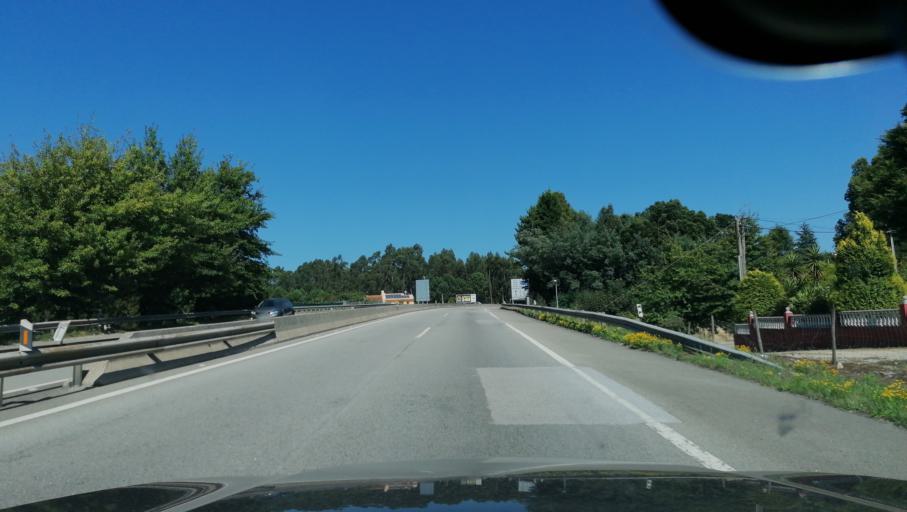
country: PT
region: Aveiro
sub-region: Santa Maria da Feira
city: Feira
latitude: 40.9243
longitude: -8.5739
